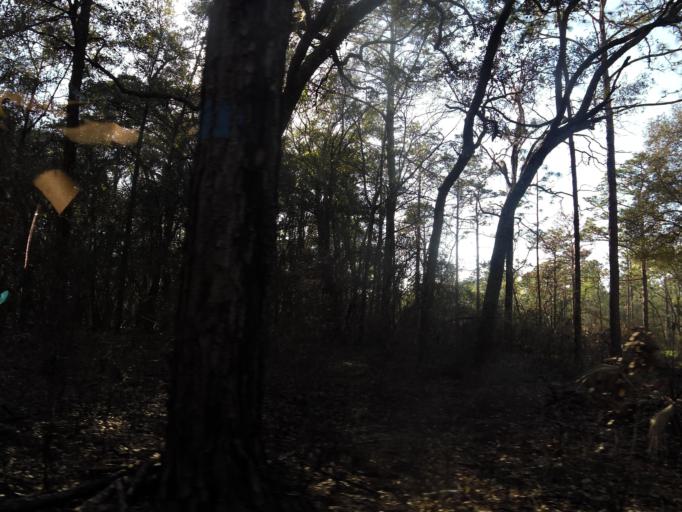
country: US
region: Florida
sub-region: Clay County
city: Middleburg
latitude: 30.1409
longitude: -81.9061
